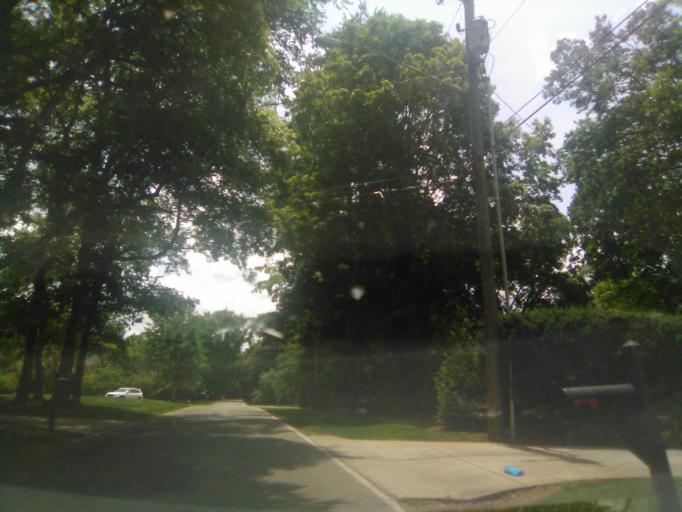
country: US
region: Tennessee
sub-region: Davidson County
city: Belle Meade
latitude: 36.0894
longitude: -86.8542
